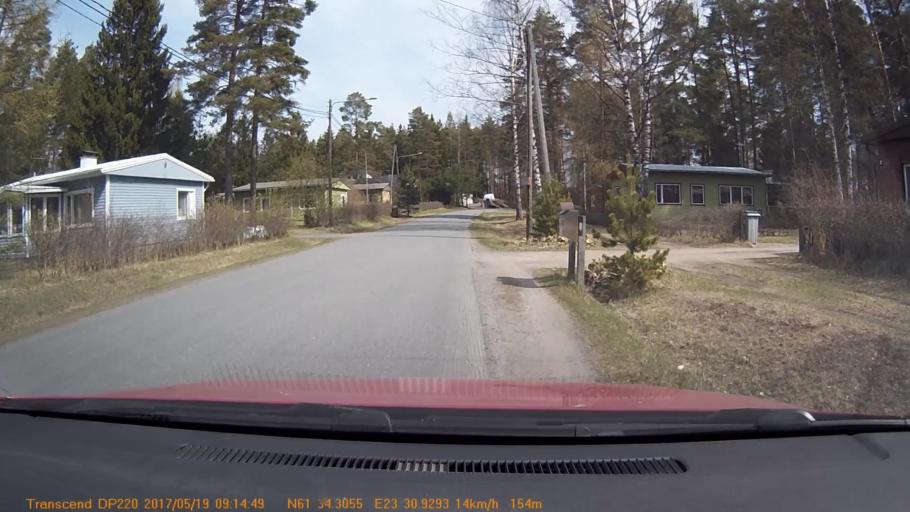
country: FI
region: Pirkanmaa
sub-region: Tampere
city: Yloejaervi
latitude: 61.5717
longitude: 23.5154
